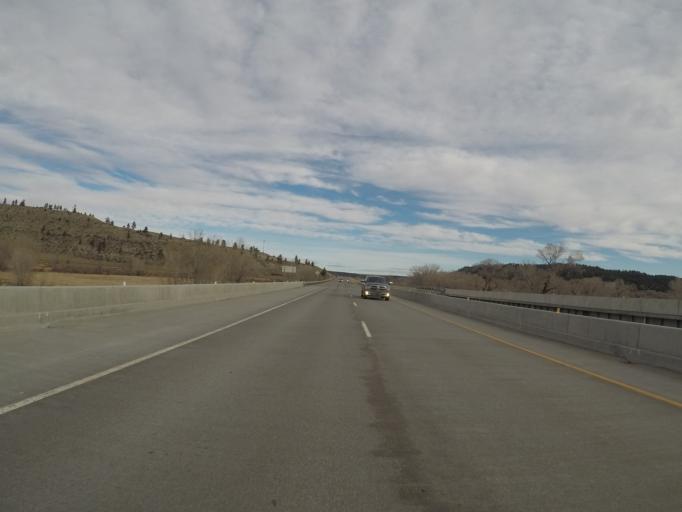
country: US
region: Montana
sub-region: Stillwater County
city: Absarokee
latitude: 45.6833
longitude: -109.4313
